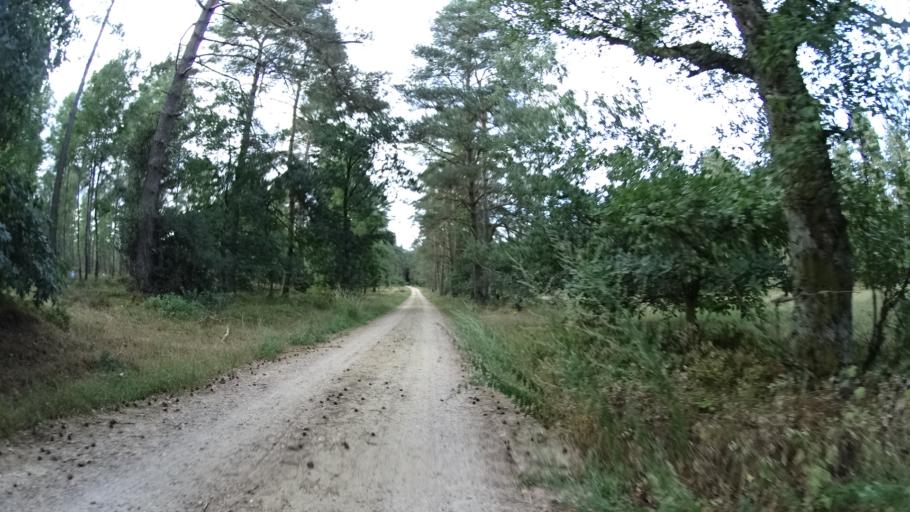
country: DE
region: Lower Saxony
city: Handeloh
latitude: 53.1904
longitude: 9.8836
